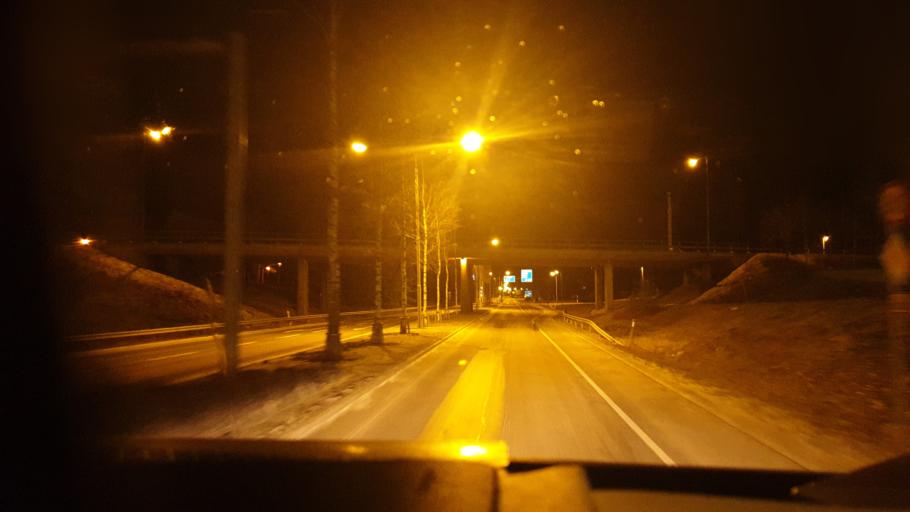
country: FI
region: Southern Ostrobothnia
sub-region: Kuusiokunnat
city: Alavus
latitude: 62.5938
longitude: 23.6131
